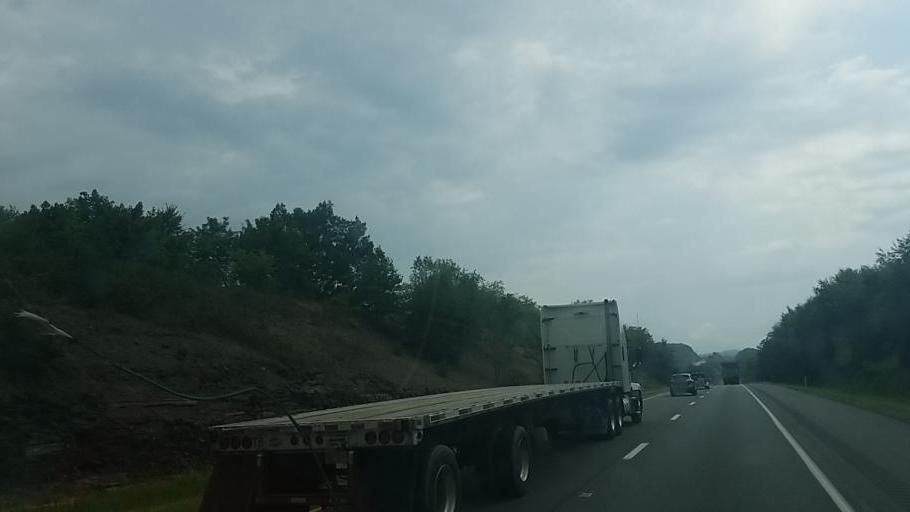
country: US
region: Pennsylvania
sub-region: Juniata County
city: Mifflintown
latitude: 40.5572
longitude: -77.2856
